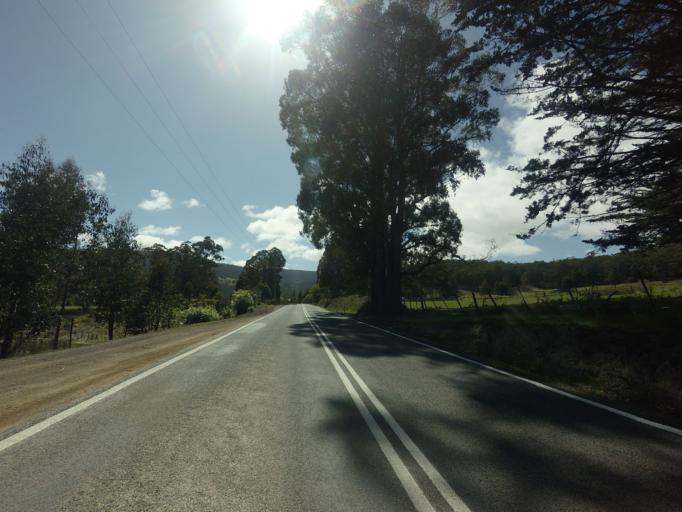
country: AU
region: Tasmania
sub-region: Derwent Valley
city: New Norfolk
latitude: -42.6900
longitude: 146.7165
